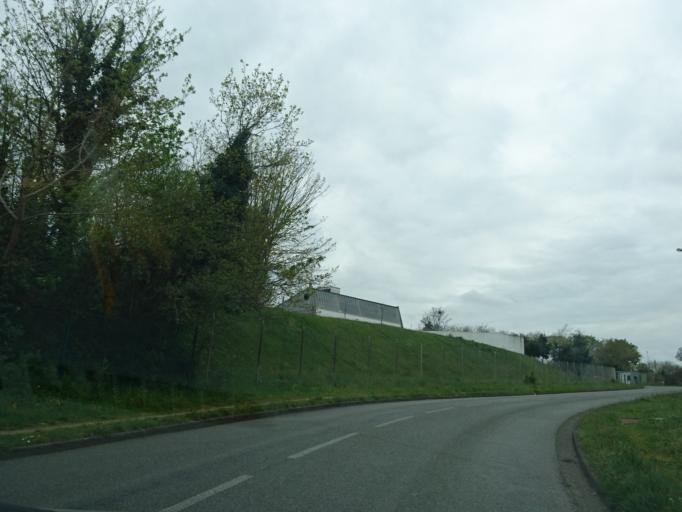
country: FR
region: Brittany
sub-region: Departement du Finistere
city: Roscanvel
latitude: 48.3612
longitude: -4.5573
